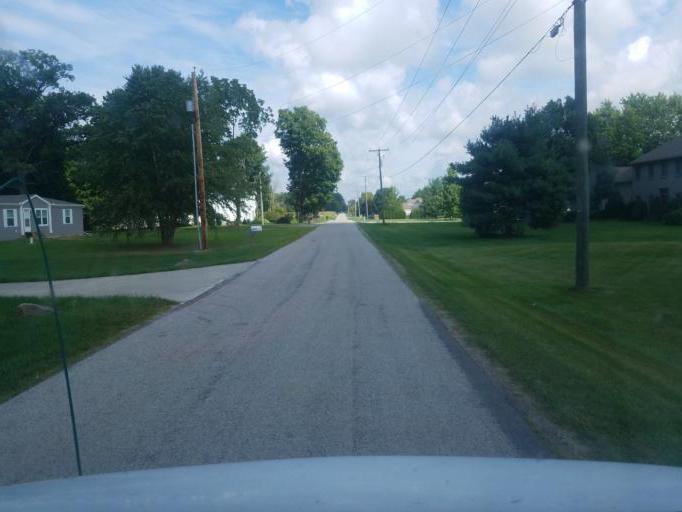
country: US
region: Ohio
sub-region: Marion County
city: Marion
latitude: 40.5114
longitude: -83.0838
